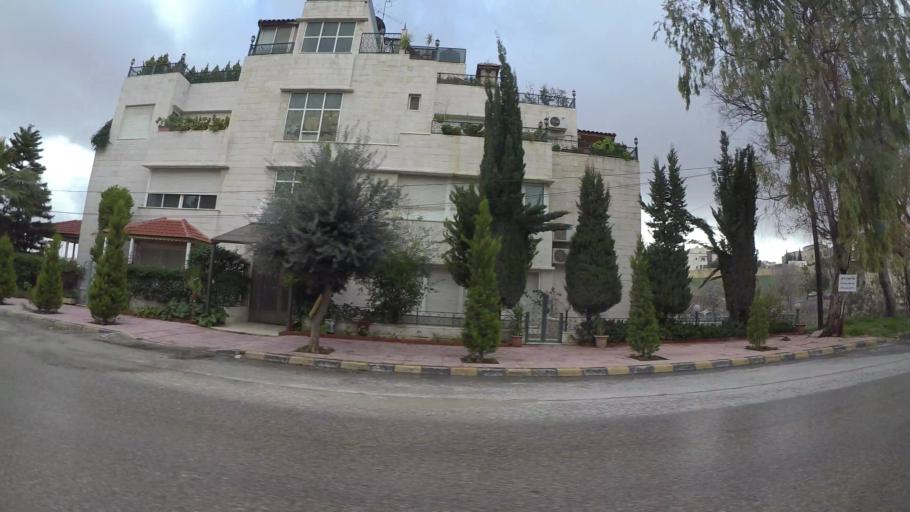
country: JO
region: Amman
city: Al Bunayyat ash Shamaliyah
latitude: 31.9471
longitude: 35.8868
